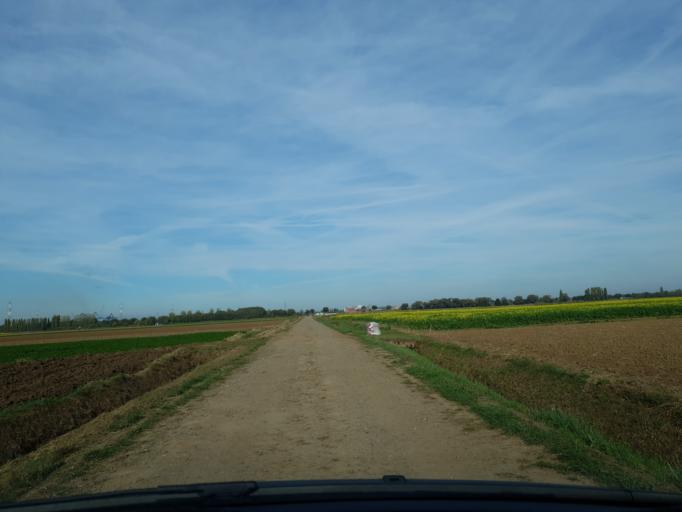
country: BE
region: Flanders
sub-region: Provincie Antwerpen
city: Stabroek
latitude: 51.3092
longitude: 4.3711
